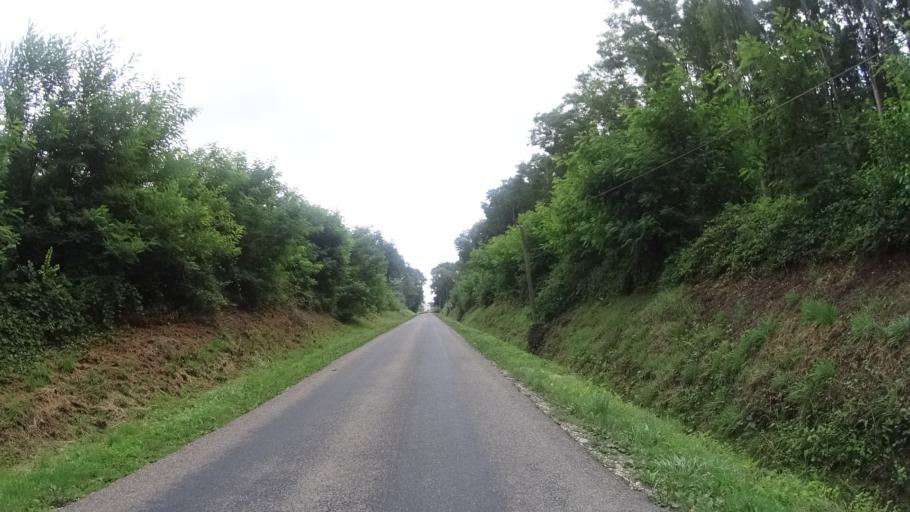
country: FR
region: Champagne-Ardenne
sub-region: Departement de l'Aube
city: Ervy-le-Chatel
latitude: 48.0718
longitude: 3.9528
